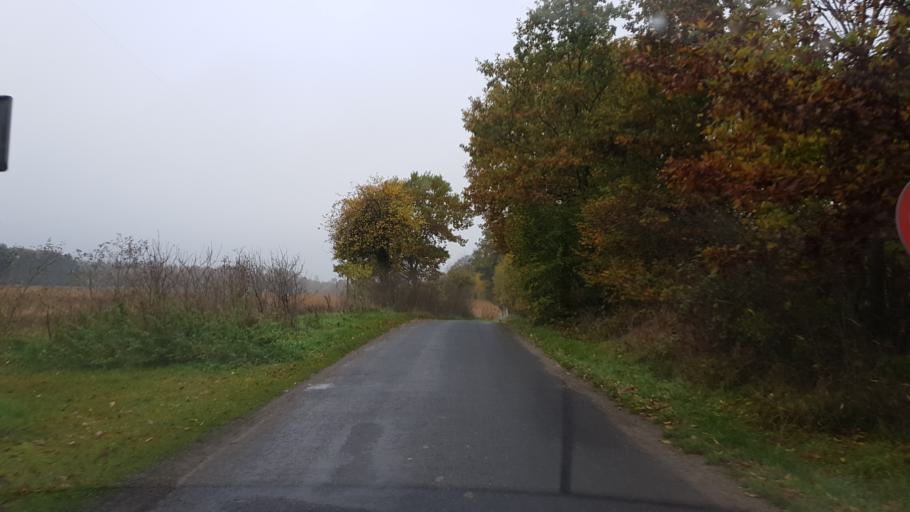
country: PL
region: West Pomeranian Voivodeship
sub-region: Powiat gryfinski
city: Chojna
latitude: 53.0471
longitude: 14.4791
